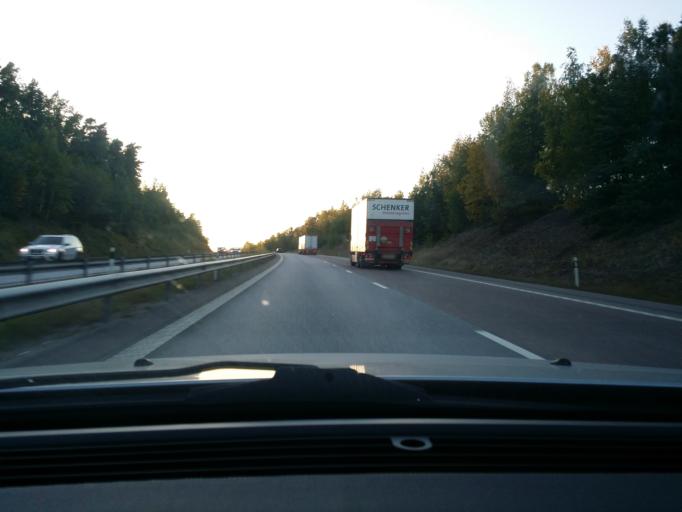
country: SE
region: Uppsala
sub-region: Habo Kommun
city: Balsta
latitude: 59.5768
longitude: 17.5402
